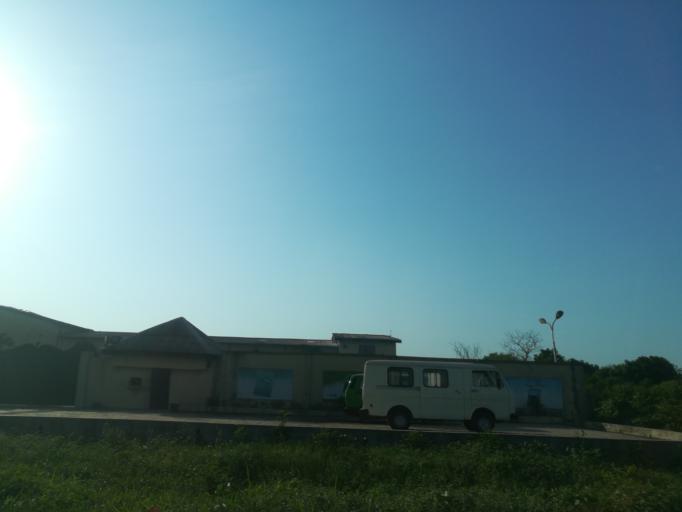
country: NG
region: Ogun
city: Abeokuta
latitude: 7.1855
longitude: 3.2819
